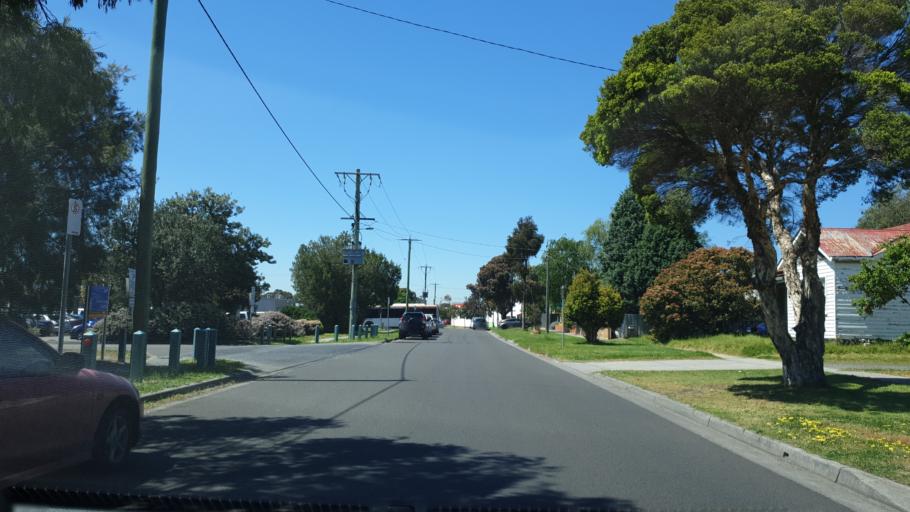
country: AU
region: Victoria
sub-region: Casey
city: Cranbourne
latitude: -38.1002
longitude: 145.2802
